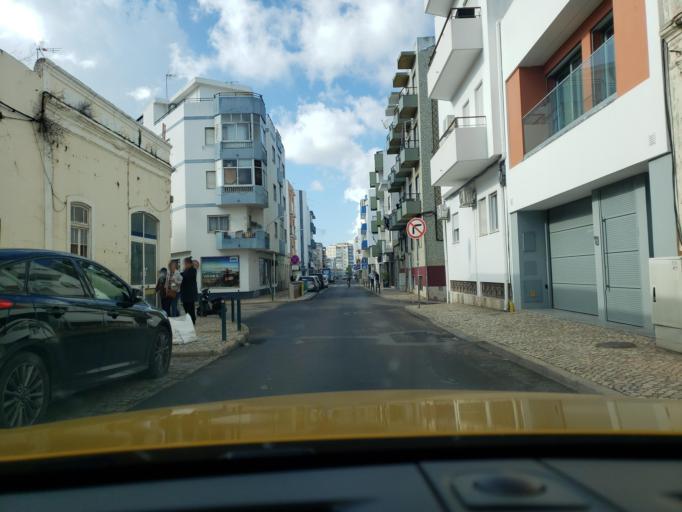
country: PT
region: Faro
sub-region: Portimao
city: Portimao
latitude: 37.1419
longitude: -8.5361
